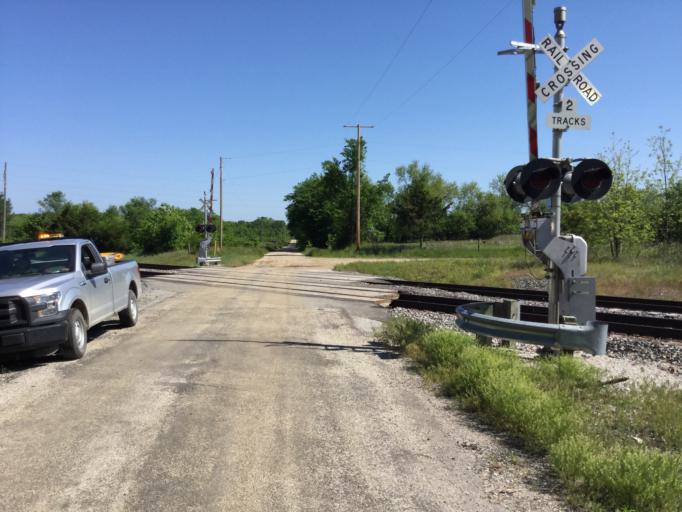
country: US
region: Kansas
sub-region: Labette County
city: Oswego
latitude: 37.2324
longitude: -95.1856
